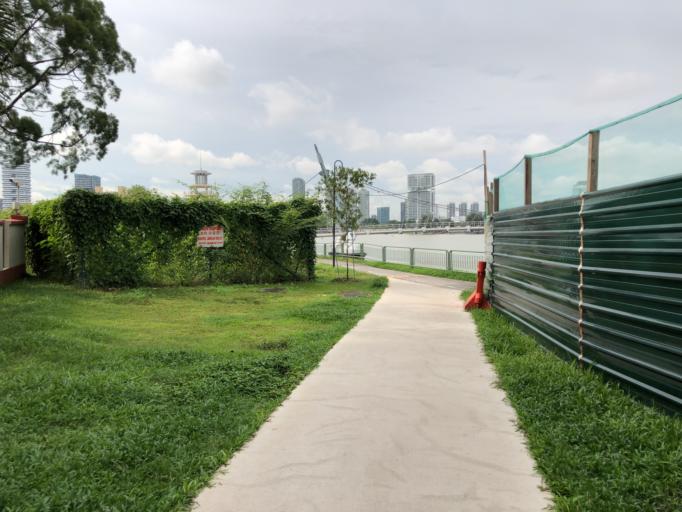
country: SG
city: Singapore
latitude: 1.2982
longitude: 103.8742
